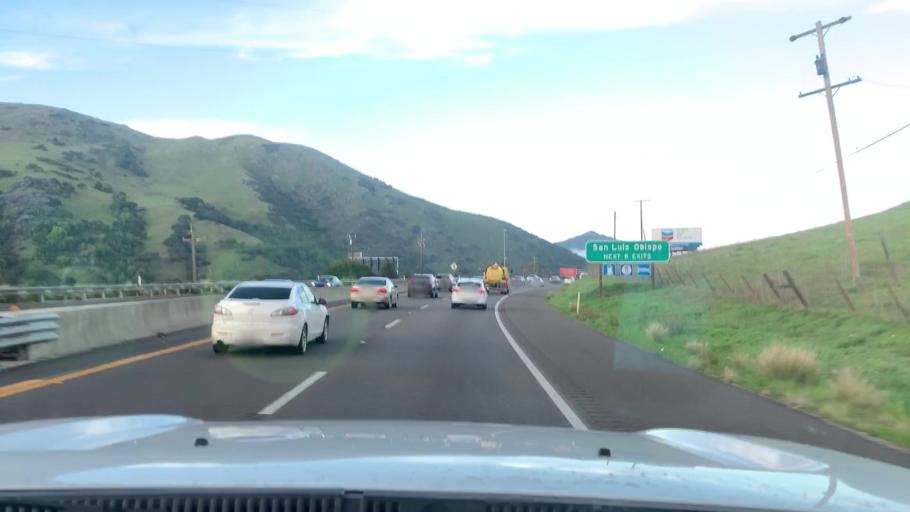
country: US
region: California
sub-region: San Luis Obispo County
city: San Luis Obispo
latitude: 35.2963
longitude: -120.6318
